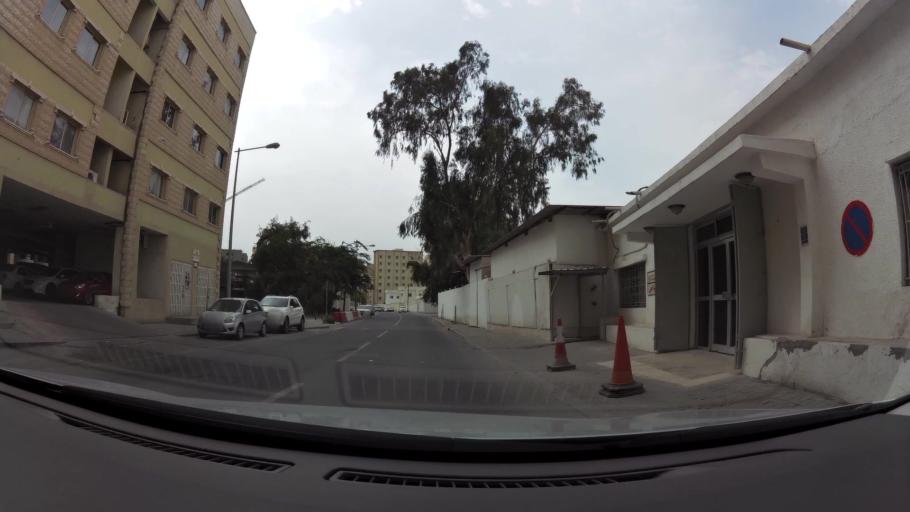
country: QA
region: Baladiyat ad Dawhah
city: Doha
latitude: 25.2861
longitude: 51.5031
